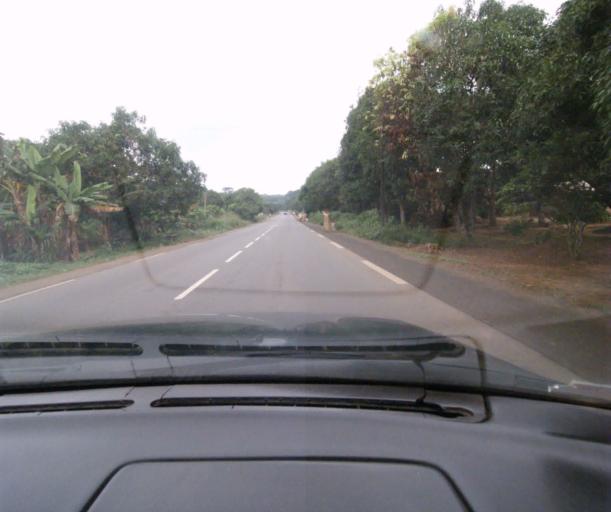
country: CM
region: Centre
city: Obala
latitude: 4.1655
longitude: 11.4958
